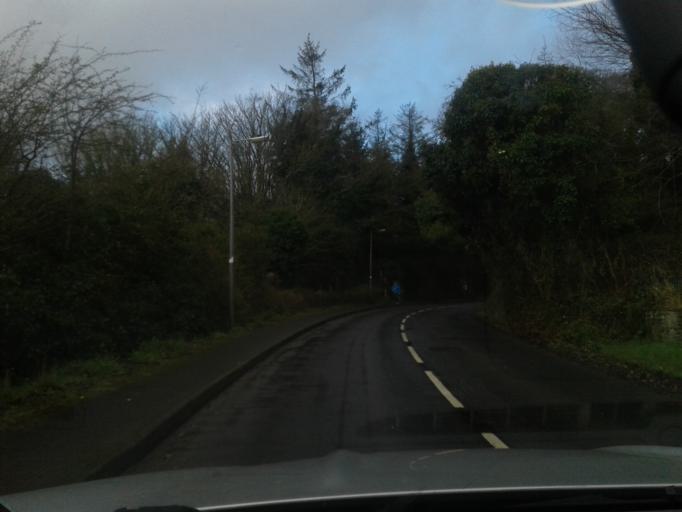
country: IE
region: Ulster
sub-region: County Donegal
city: Ramelton
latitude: 55.0383
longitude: -7.6476
